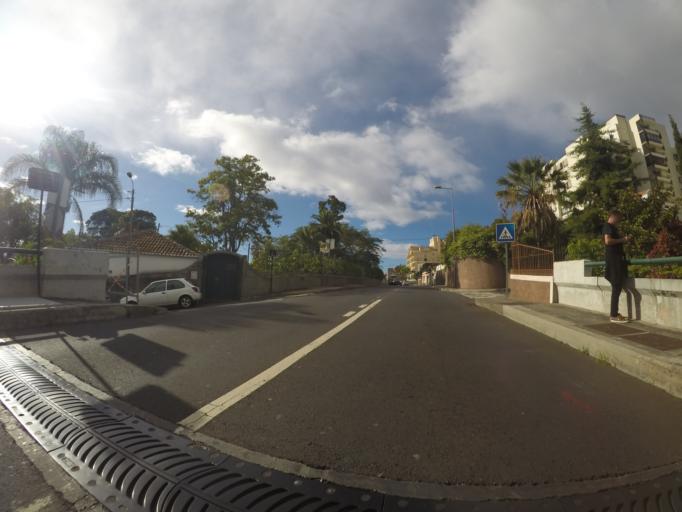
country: PT
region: Madeira
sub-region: Funchal
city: Funchal
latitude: 32.6448
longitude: -16.9252
